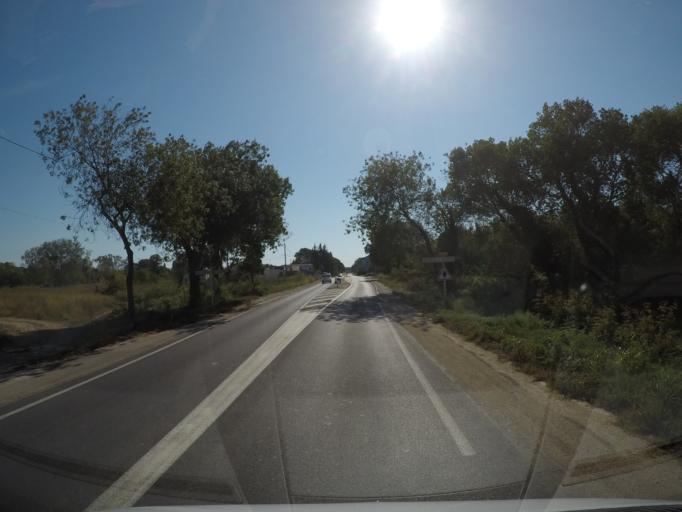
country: FR
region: Languedoc-Roussillon
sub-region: Departement du Gard
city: Moussac
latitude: 43.9786
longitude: 4.2076
